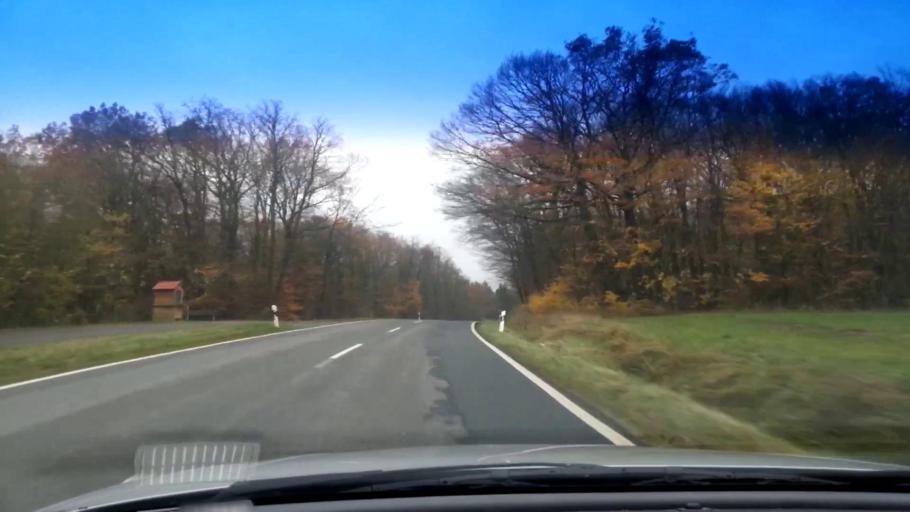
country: DE
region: Bavaria
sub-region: Upper Franconia
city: Litzendorf
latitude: 49.8906
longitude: 11.0093
